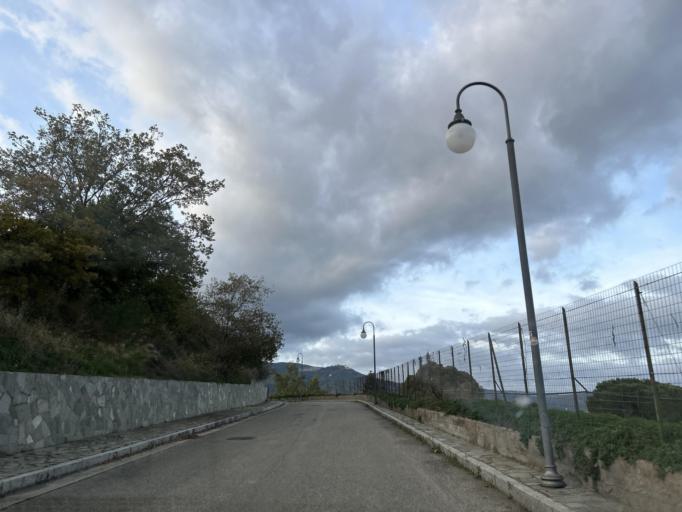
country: IT
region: Calabria
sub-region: Provincia di Catanzaro
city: Soverato Superiore
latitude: 38.7011
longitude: 16.5365
